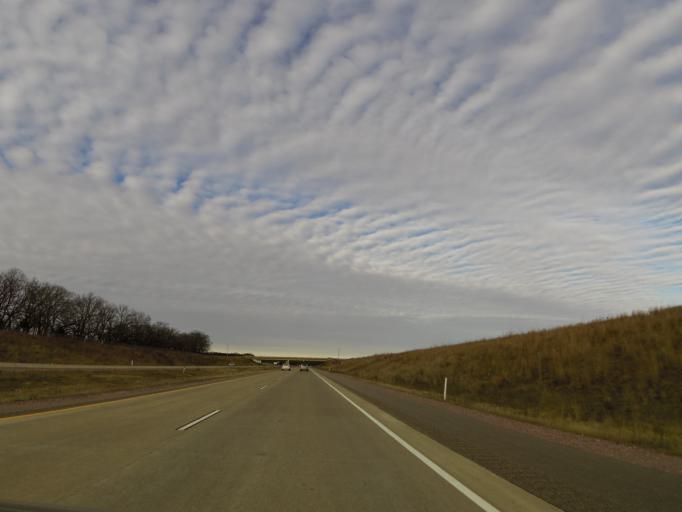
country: US
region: Wisconsin
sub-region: Sauk County
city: Lake Delton
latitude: 43.5432
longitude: -89.7870
